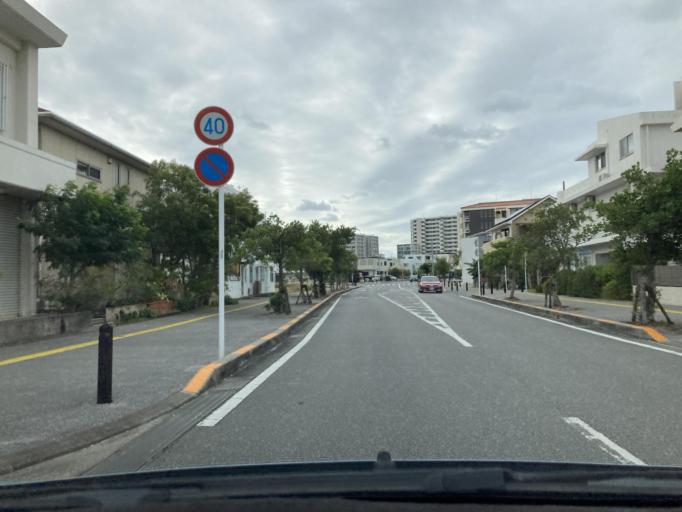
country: JP
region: Okinawa
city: Itoman
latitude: 26.1560
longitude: 127.6629
